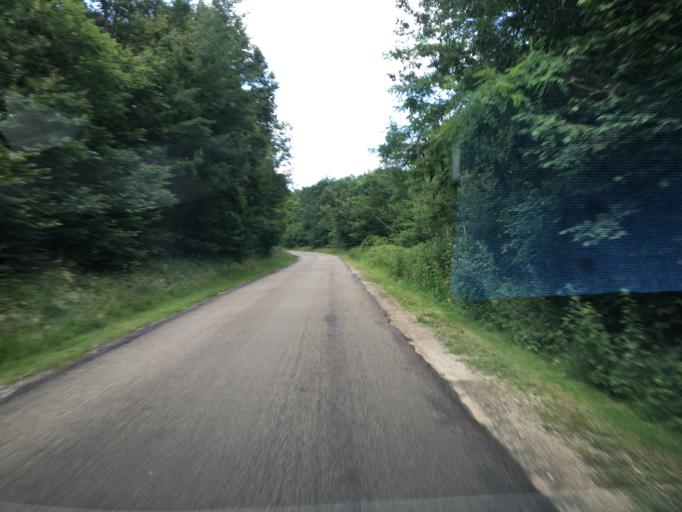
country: FR
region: Bourgogne
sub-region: Departement de l'Yonne
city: Charbuy
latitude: 47.8451
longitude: 3.4914
